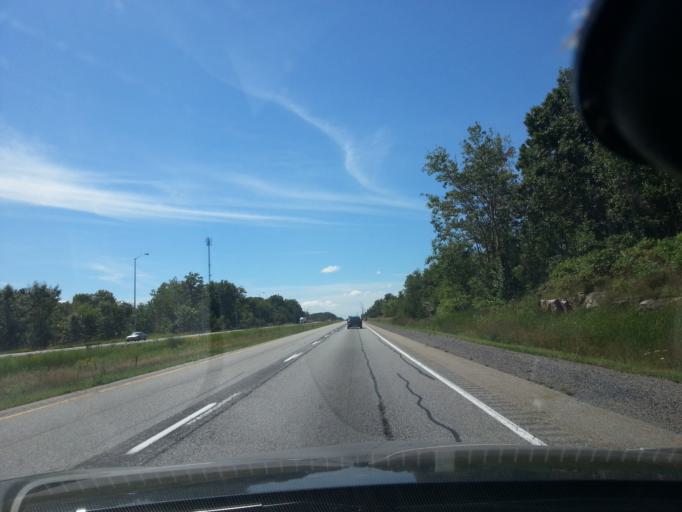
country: CA
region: Ontario
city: Gananoque
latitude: 44.3650
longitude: -76.0711
